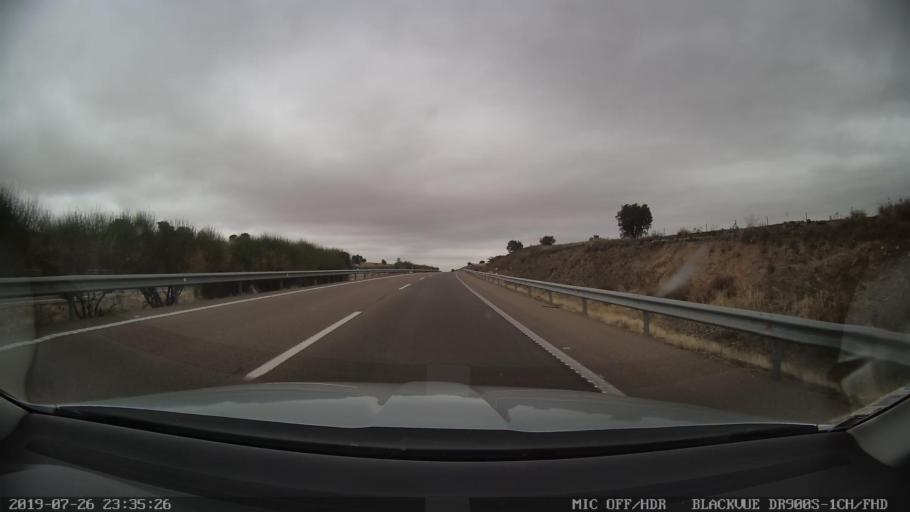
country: ES
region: Extremadura
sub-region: Provincia de Caceres
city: Santa Cruz de la Sierra
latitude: 39.3758
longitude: -5.8801
